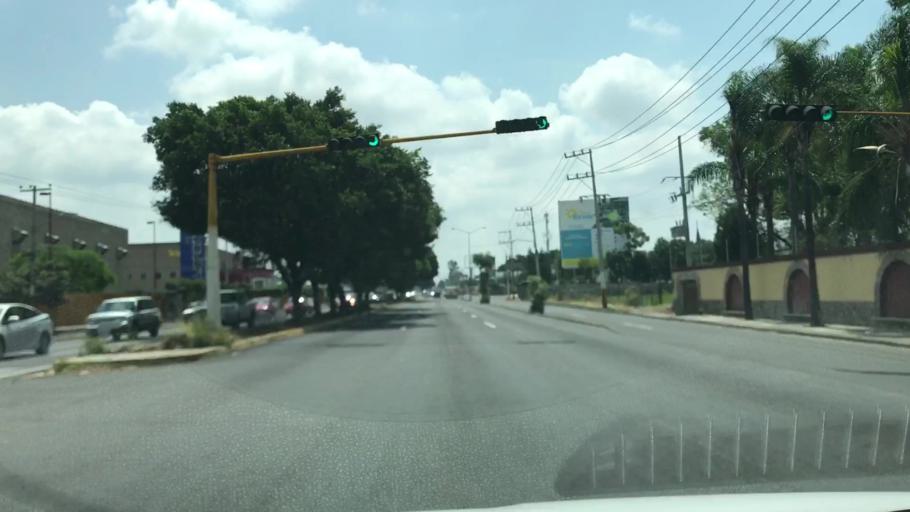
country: MX
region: Jalisco
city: Nuevo Mexico
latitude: 20.7567
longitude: -103.4288
